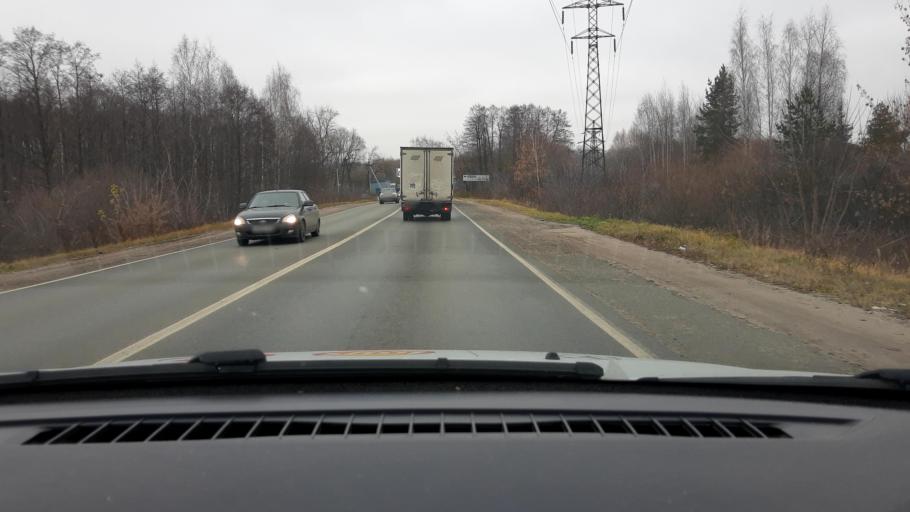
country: RU
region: Nizjnij Novgorod
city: Novaya Balakhna
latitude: 56.5155
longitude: 43.5797
